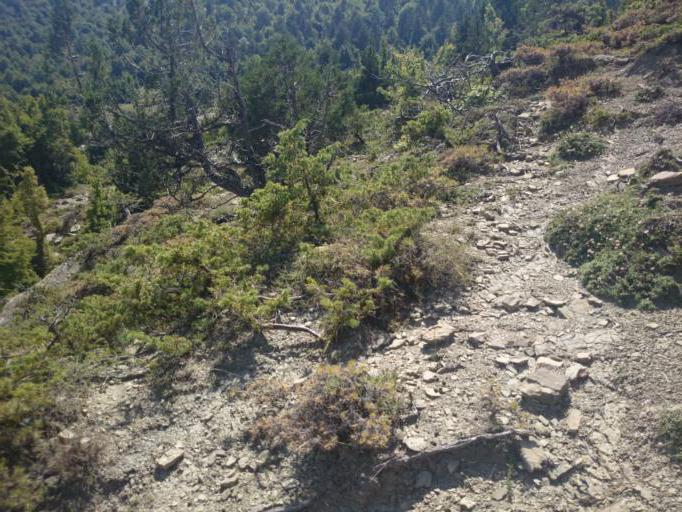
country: AL
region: Elbasan
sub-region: Rrethi i Gramshit
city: Kushove
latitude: 40.7440
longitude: 20.1562
